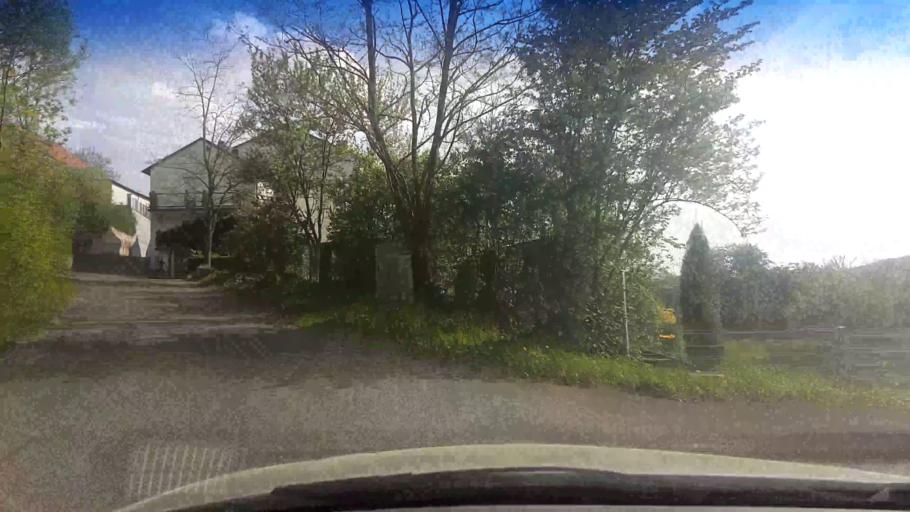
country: DE
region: Bavaria
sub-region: Upper Franconia
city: Rattelsdorf
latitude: 50.0162
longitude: 10.8835
